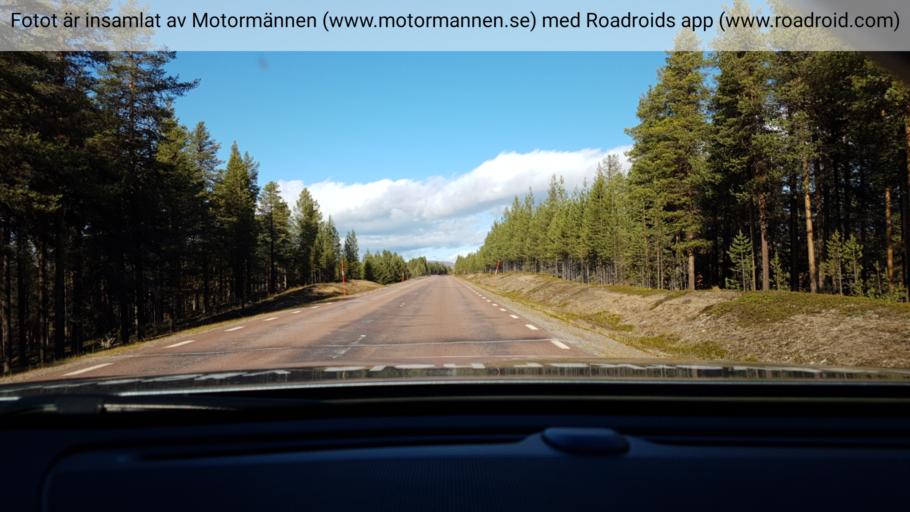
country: SE
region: Norrbotten
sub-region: Arjeplogs Kommun
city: Arjeplog
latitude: 66.0223
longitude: 18.0696
